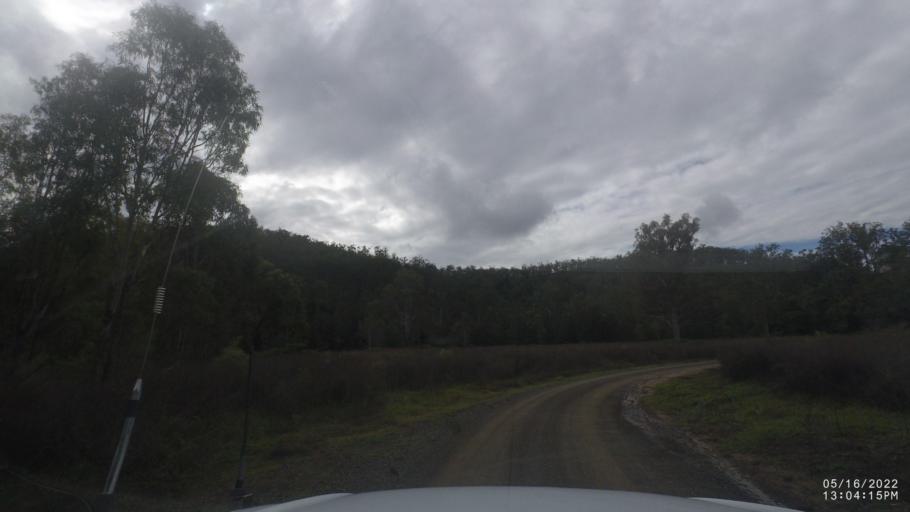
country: AU
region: Queensland
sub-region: Logan
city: Cedar Vale
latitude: -27.8666
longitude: 152.8398
